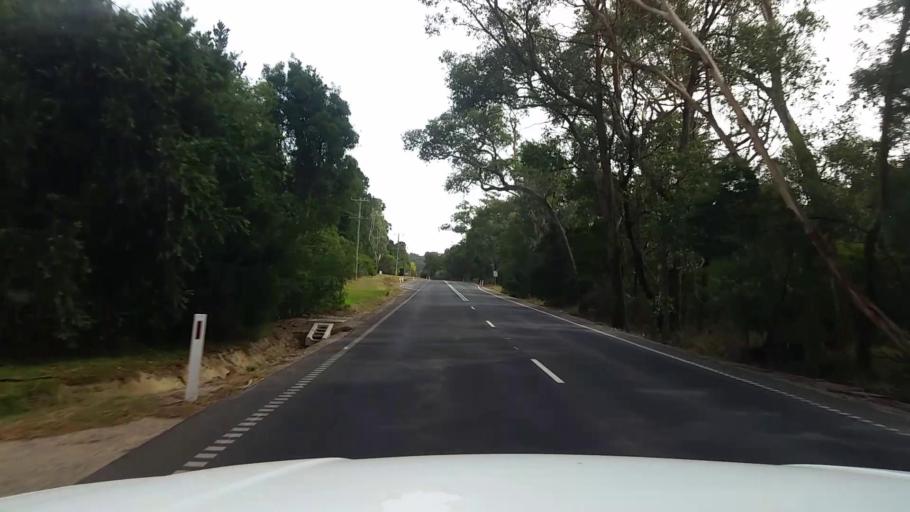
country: AU
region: Victoria
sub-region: Mornington Peninsula
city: Balnarring
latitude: -38.3460
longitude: 145.1021
